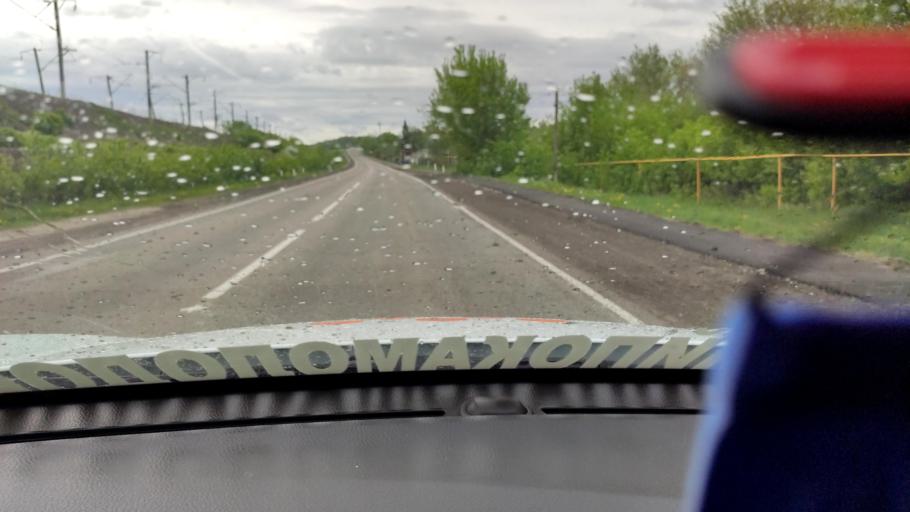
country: RU
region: Voronezj
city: Imeni Pervogo Maya
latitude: 50.7568
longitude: 39.3889
